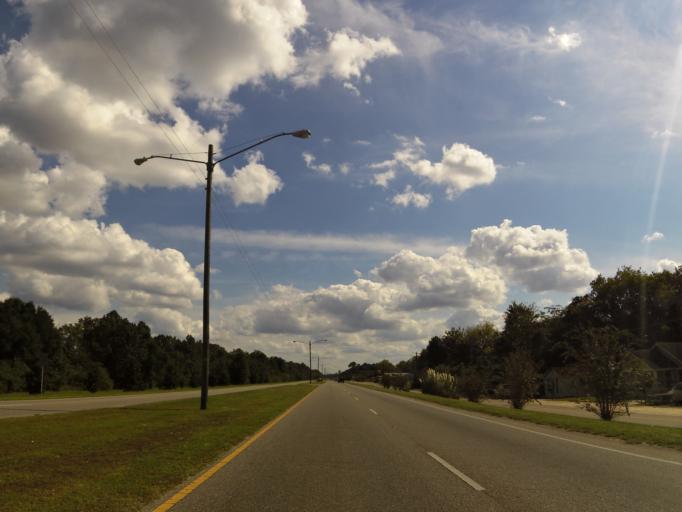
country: US
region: Alabama
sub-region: Dallas County
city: Selmont-West Selmont
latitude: 32.3929
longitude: -87.0139
